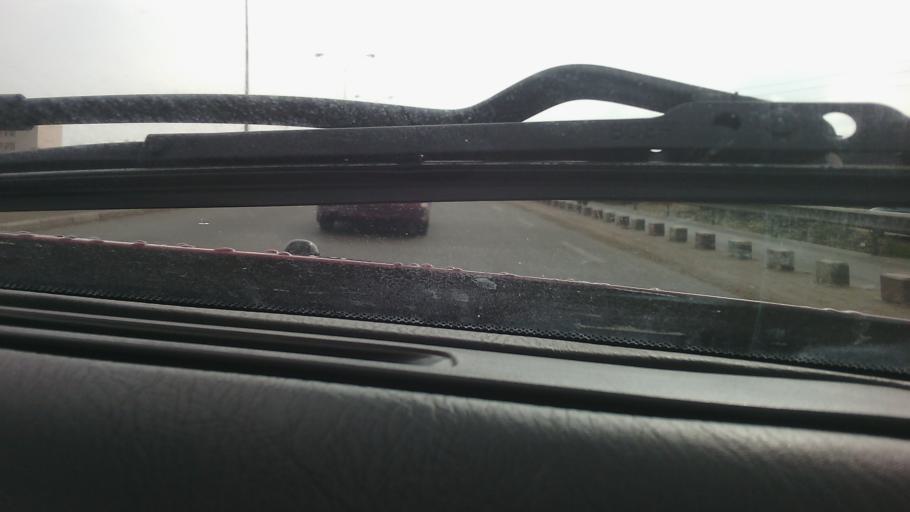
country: BJ
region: Littoral
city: Cotonou
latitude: 6.3706
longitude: 2.5178
